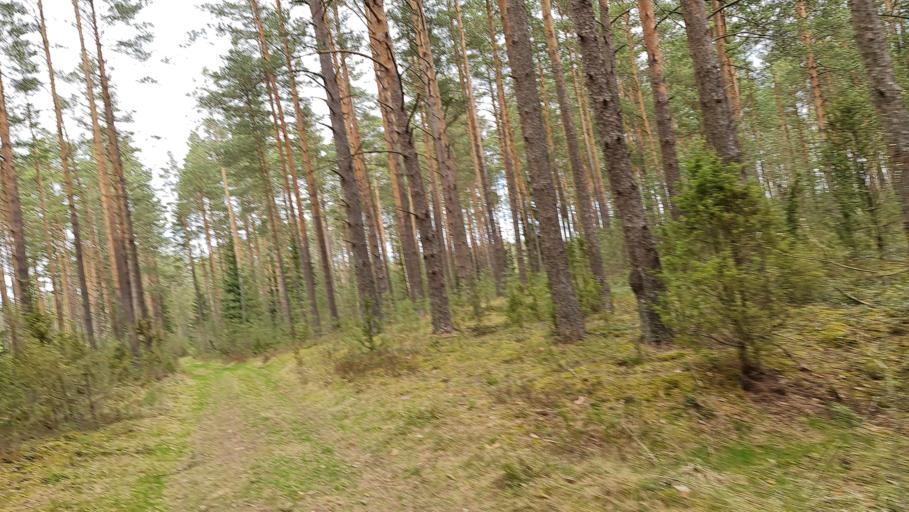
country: BY
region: Vitebsk
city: Byahoml'
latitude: 54.7365
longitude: 28.0328
